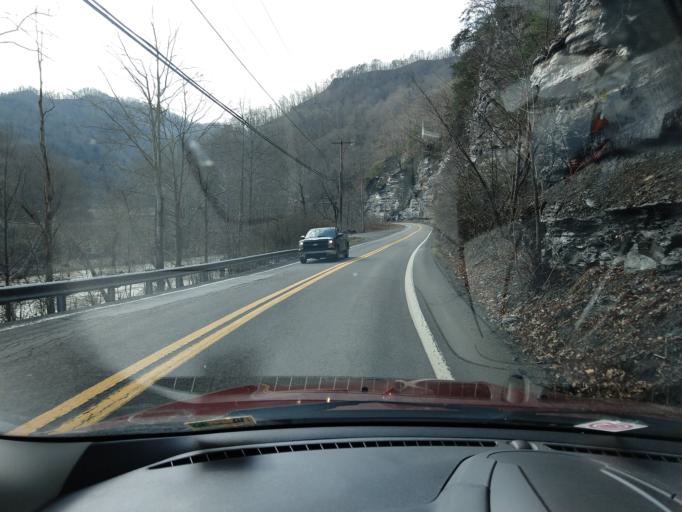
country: US
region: West Virginia
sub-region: McDowell County
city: Welch
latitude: 37.3631
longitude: -81.7995
